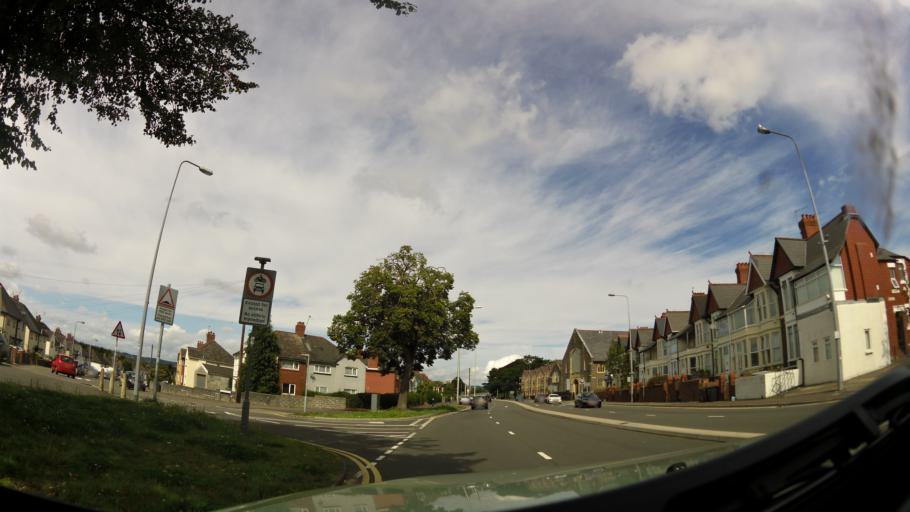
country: GB
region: Wales
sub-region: Cardiff
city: Cardiff
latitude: 51.4991
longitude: -3.1941
